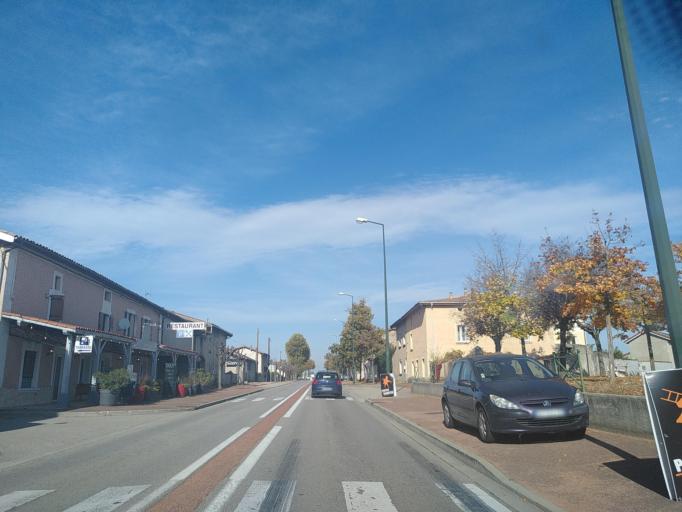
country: FR
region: Rhone-Alpes
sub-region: Departement de la Drome
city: Andancette
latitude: 45.2600
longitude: 4.8234
